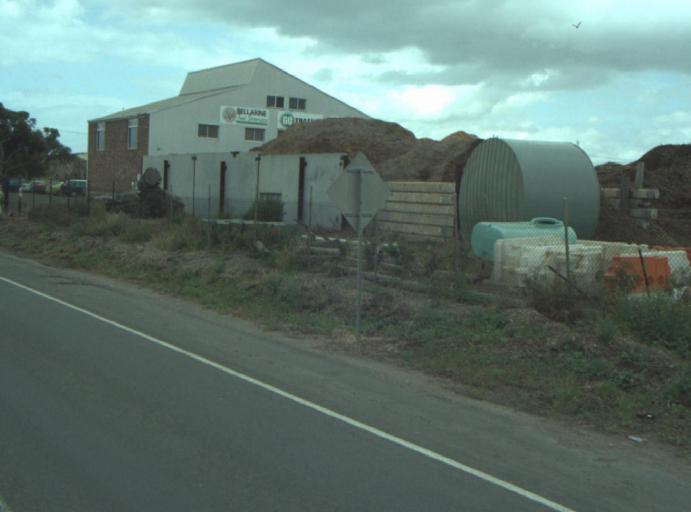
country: AU
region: Victoria
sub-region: Greater Geelong
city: Leopold
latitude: -38.1658
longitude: 144.4239
